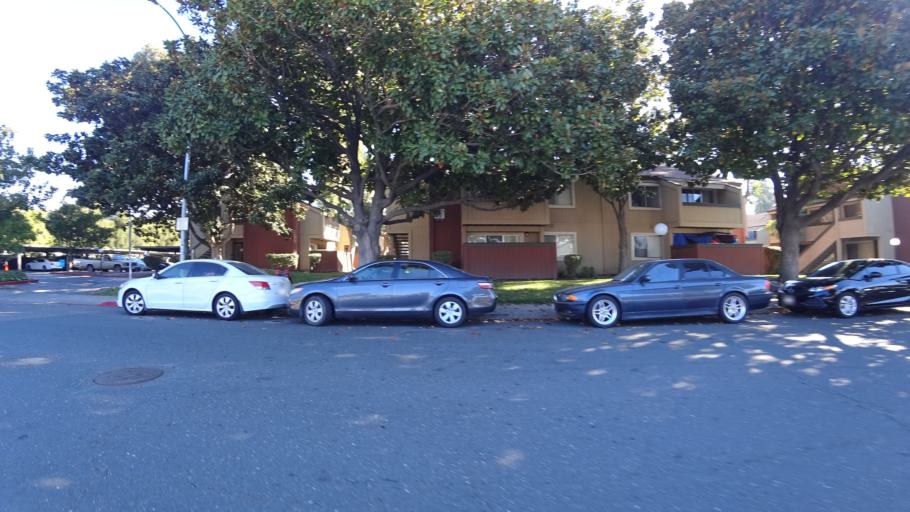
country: US
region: California
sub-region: Alameda County
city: Union City
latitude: 37.6055
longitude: -122.0549
